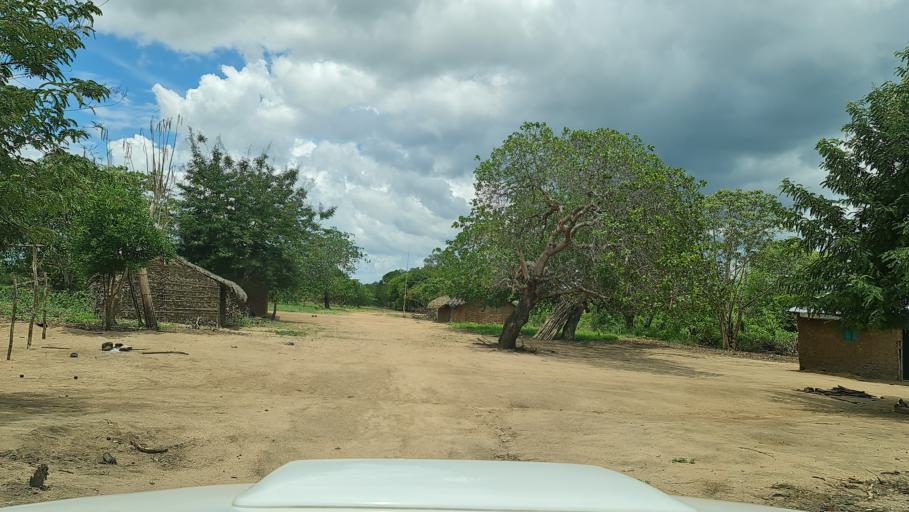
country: MZ
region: Nampula
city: Ilha de Mocambique
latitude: -15.5173
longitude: 40.2018
